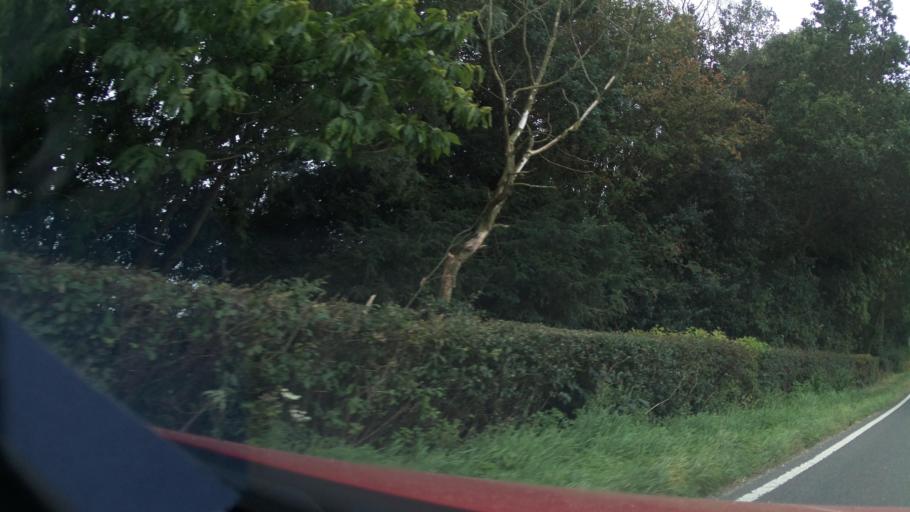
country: GB
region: England
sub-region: Derbyshire
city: Bradley
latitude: 53.0153
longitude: -1.6697
